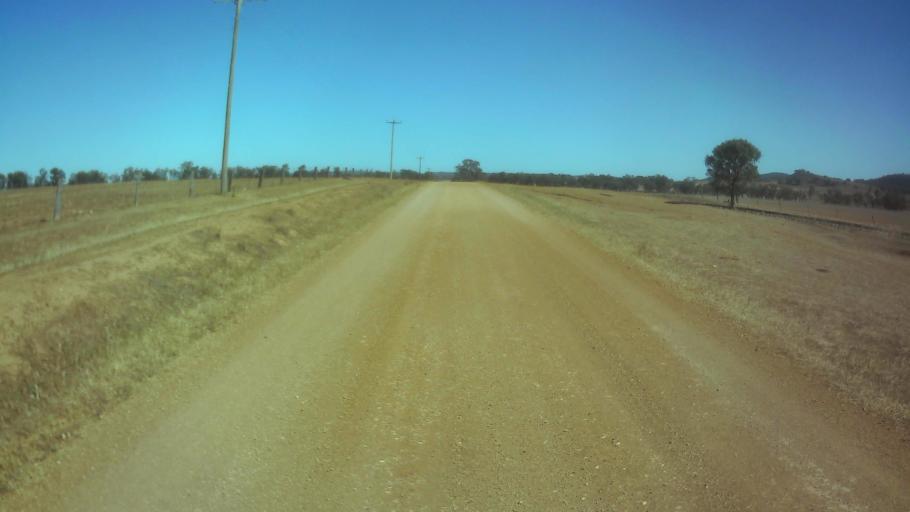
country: AU
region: New South Wales
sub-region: Weddin
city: Grenfell
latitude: -33.9508
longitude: 148.2991
